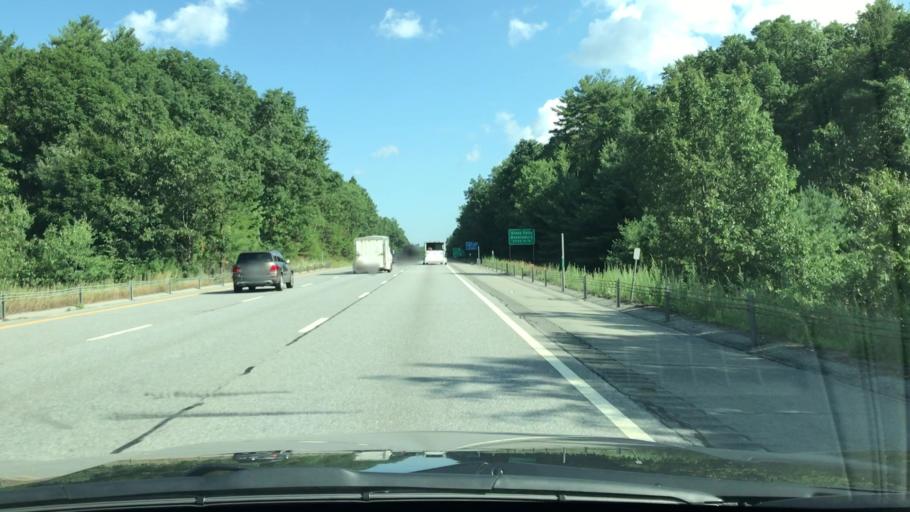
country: US
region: New York
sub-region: Warren County
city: Glens Falls North
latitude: 43.3458
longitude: -73.6942
